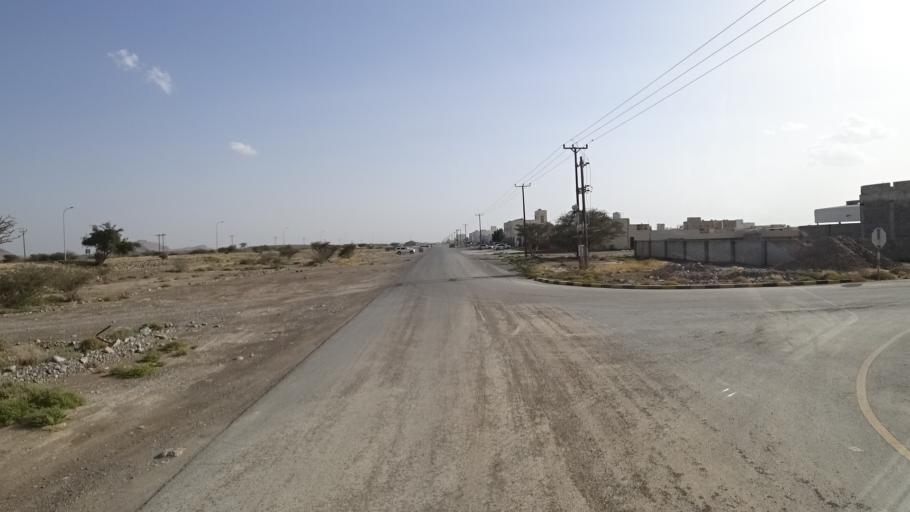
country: OM
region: Muhafazat ad Dakhiliyah
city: Izki
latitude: 22.8621
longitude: 57.7584
